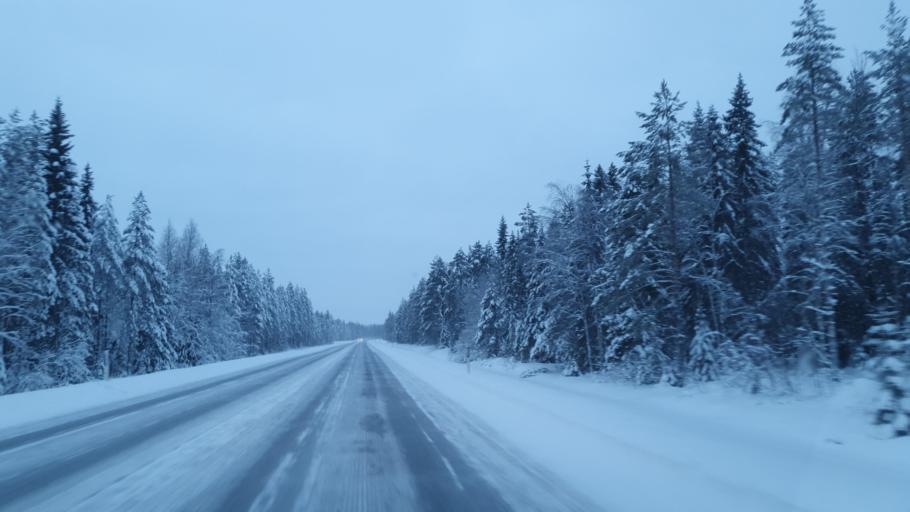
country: FI
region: Kainuu
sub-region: Kajaani
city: Vaala
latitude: 64.5979
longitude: 26.7019
